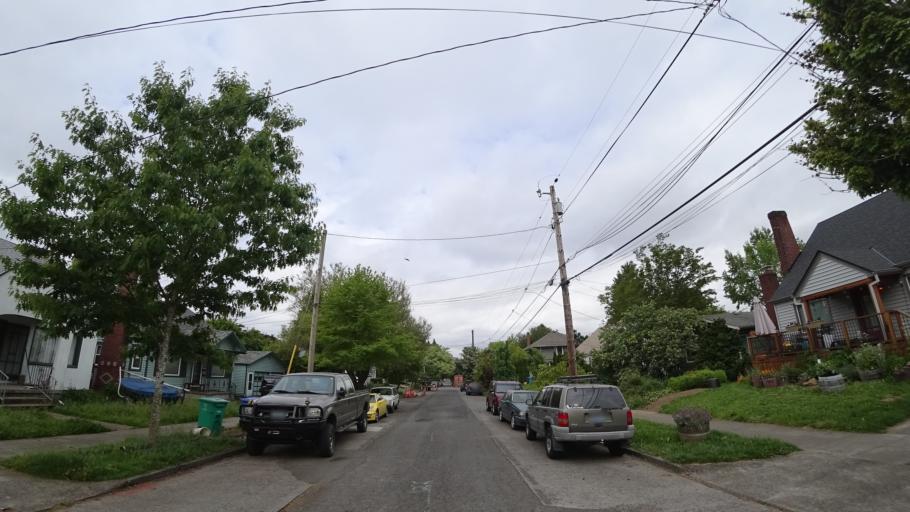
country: US
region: Oregon
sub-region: Clackamas County
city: Milwaukie
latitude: 45.4991
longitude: -122.6252
